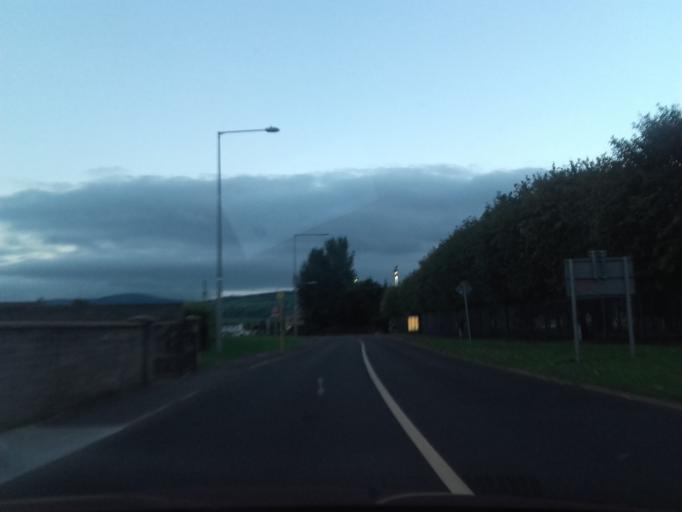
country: IE
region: Leinster
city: Tallaght
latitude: 53.2916
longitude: -6.3874
